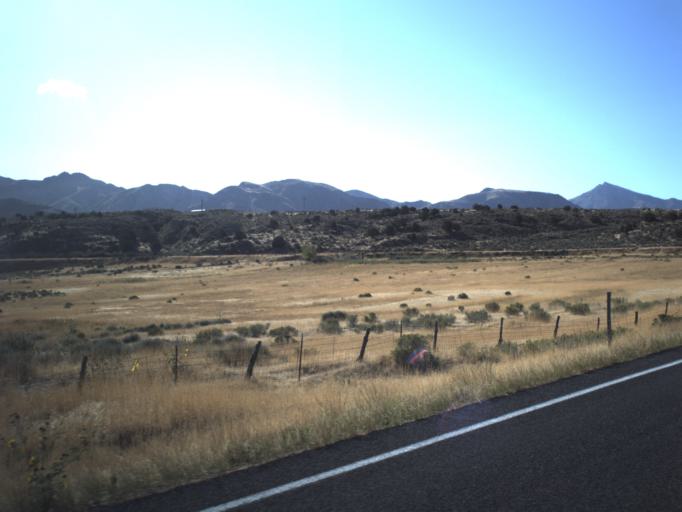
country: US
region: Utah
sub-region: Millard County
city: Delta
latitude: 39.5210
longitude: -112.2733
